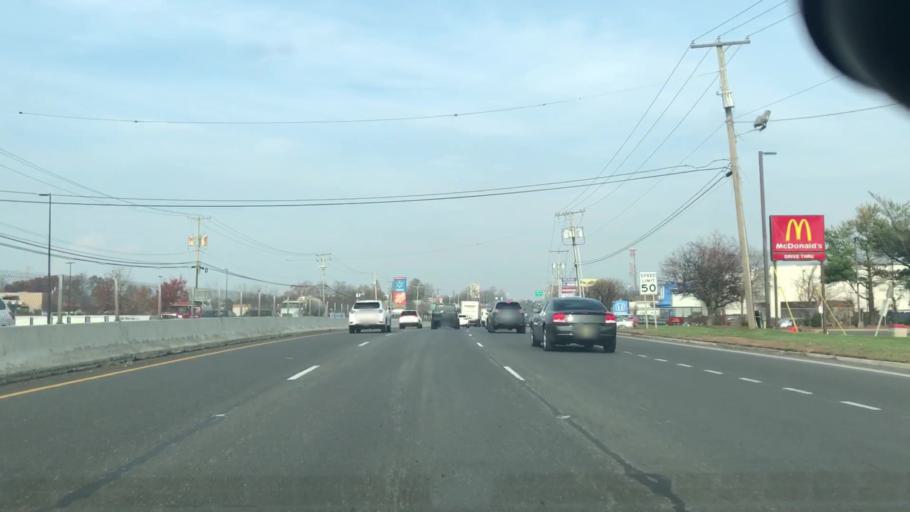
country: US
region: New Jersey
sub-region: Middlesex County
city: Madison Park
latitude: 40.4473
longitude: -74.2995
